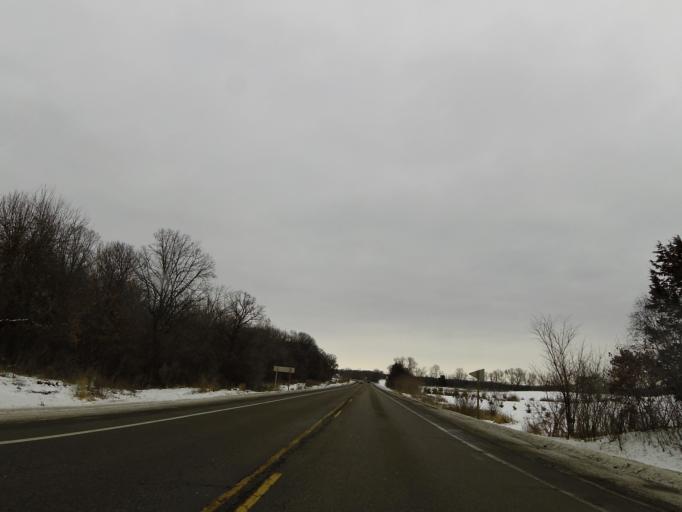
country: US
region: Minnesota
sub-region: Washington County
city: Stillwater
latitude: 45.0716
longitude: -92.7700
